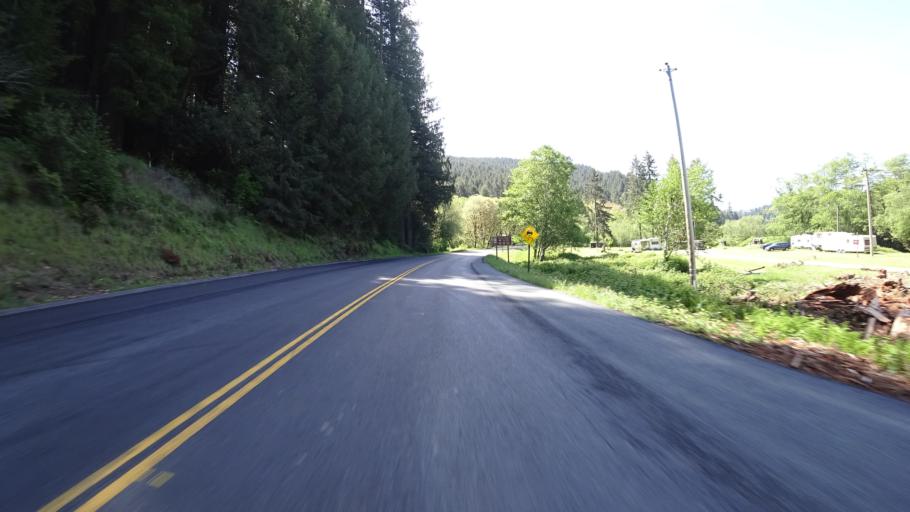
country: US
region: California
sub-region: Humboldt County
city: Westhaven-Moonstone
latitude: 41.3298
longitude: -124.0299
